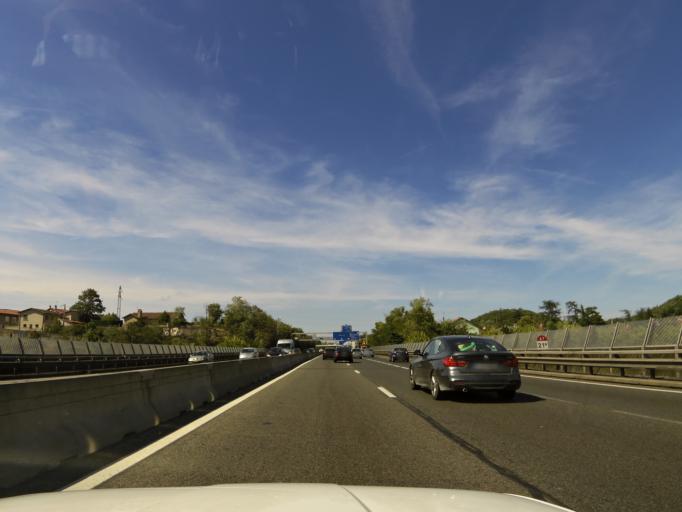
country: FR
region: Rhone-Alpes
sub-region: Departement de l'Isere
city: Chasse-sur-Rhone
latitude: 45.5795
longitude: 4.8028
